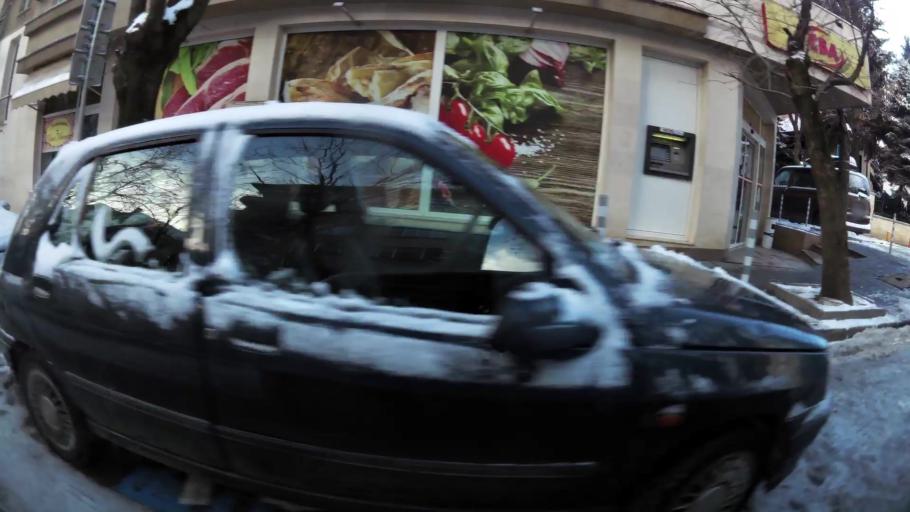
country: BG
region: Sofia-Capital
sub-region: Stolichna Obshtina
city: Sofia
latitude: 42.6718
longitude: 23.3263
